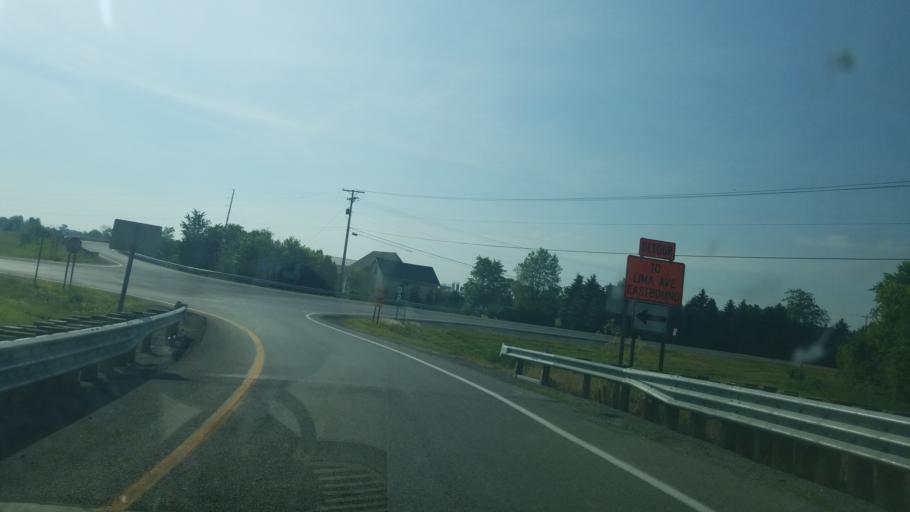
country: US
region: Ohio
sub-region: Hancock County
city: Findlay
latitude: 40.9887
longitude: -83.6513
